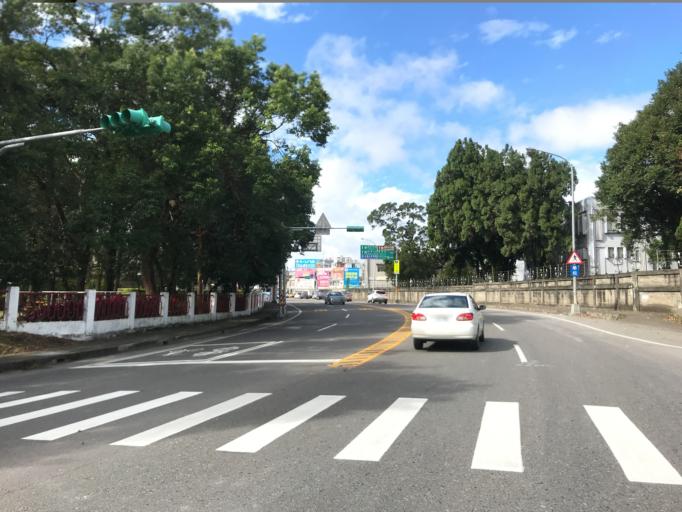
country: TW
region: Taiwan
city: Daxi
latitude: 24.8476
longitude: 121.2461
